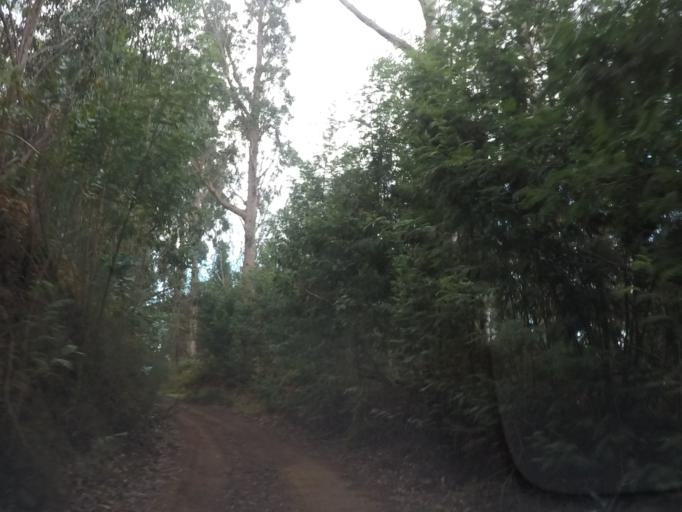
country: PT
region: Madeira
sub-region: Funchal
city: Nossa Senhora do Monte
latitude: 32.6786
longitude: -16.8778
